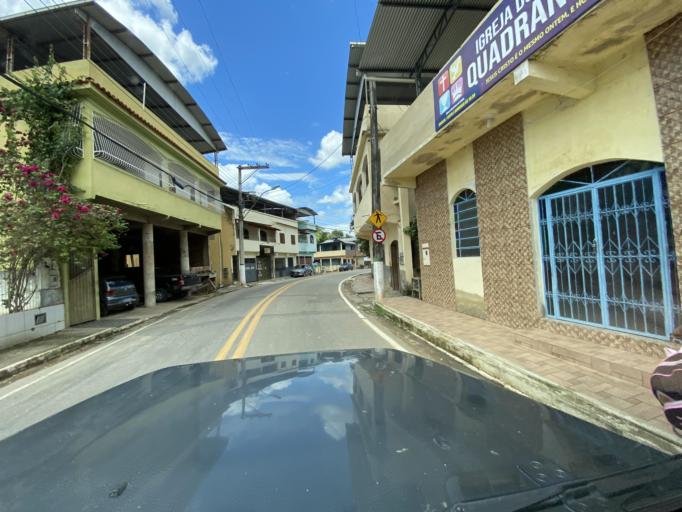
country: BR
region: Espirito Santo
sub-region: Jeronimo Monteiro
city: Jeronimo Monteiro
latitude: -20.7930
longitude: -41.4006
